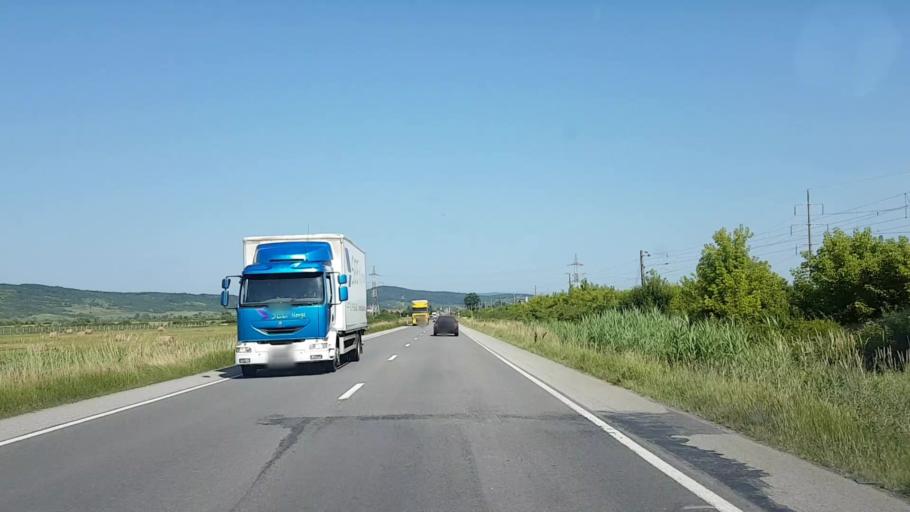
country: RO
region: Bistrita-Nasaud
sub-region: Comuna Sintereag
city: Cociu
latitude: 47.1819
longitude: 24.2486
